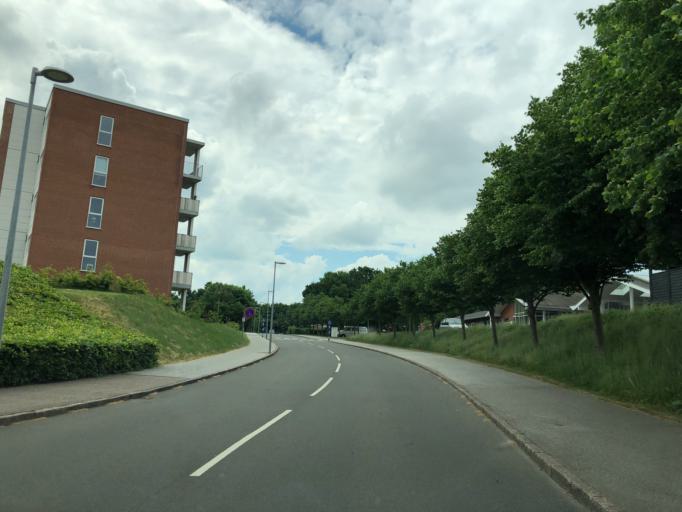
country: DK
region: Central Jutland
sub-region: Struer Kommune
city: Struer
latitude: 56.4918
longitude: 8.5730
